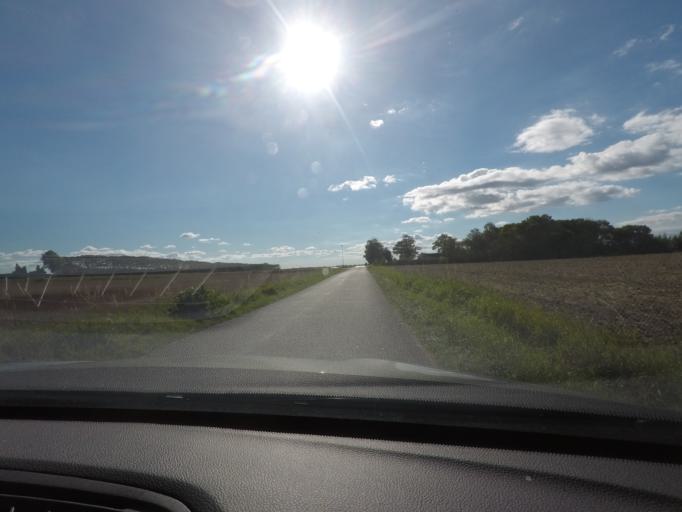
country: DK
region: Zealand
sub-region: Lolland Kommune
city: Maribo
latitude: 54.9745
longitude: 11.5228
